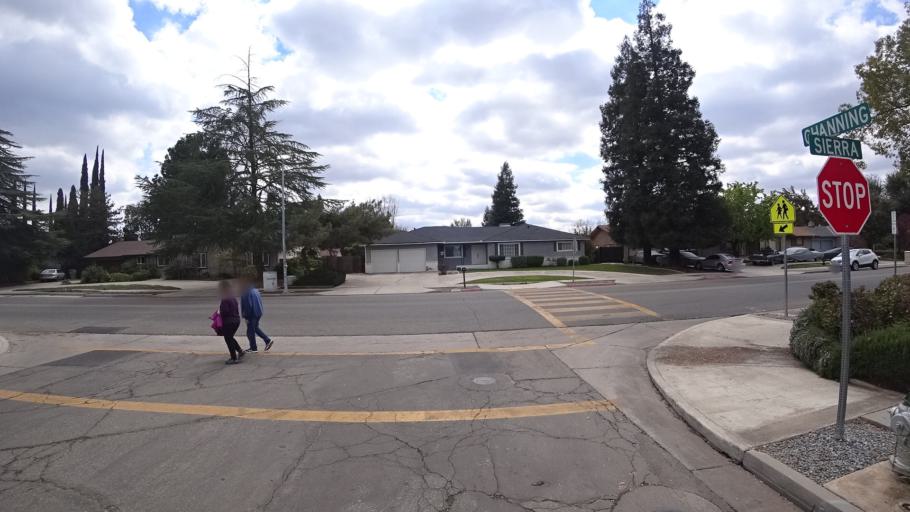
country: US
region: California
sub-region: Fresno County
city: Fresno
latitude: 36.8301
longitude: -119.8236
